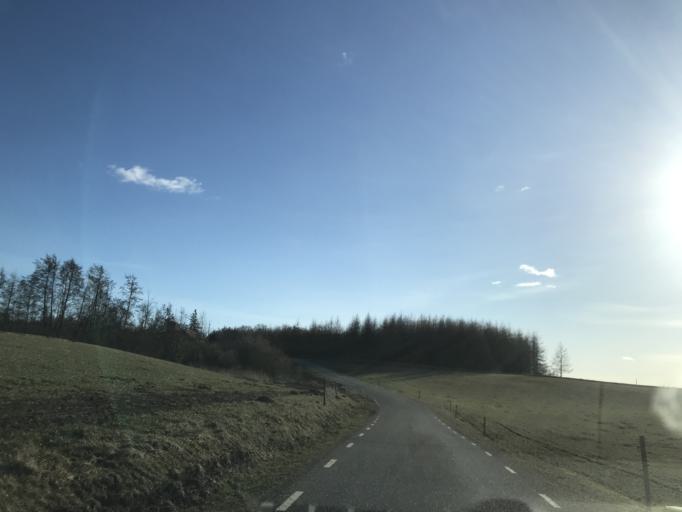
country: SE
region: Skane
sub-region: Ystads Kommun
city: Ystad
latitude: 55.5546
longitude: 13.8078
